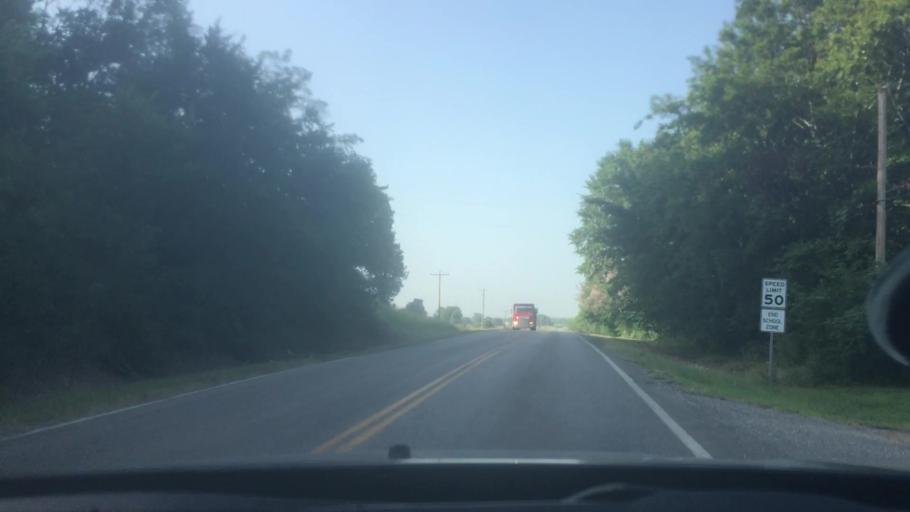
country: US
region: Oklahoma
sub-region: Coal County
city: Coalgate
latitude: 34.3674
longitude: -96.4246
